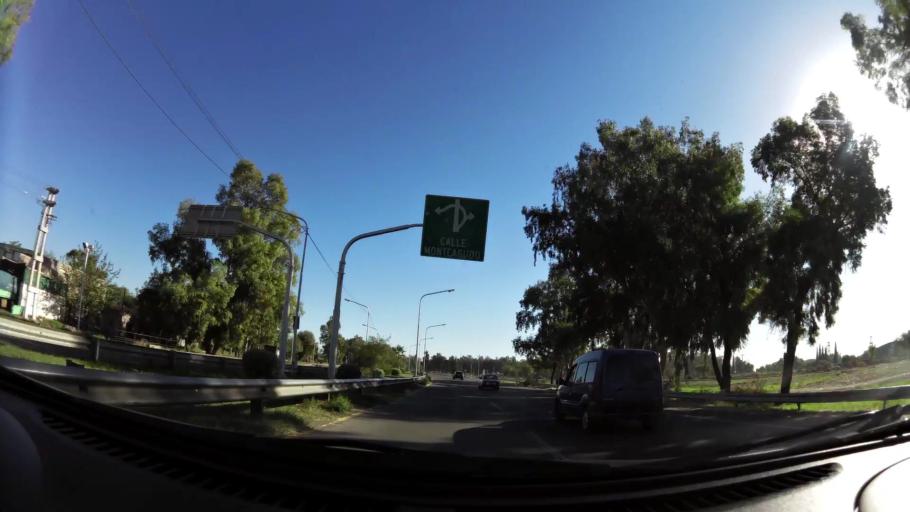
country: AR
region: Mendoza
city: Las Heras
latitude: -32.8465
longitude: -68.8025
